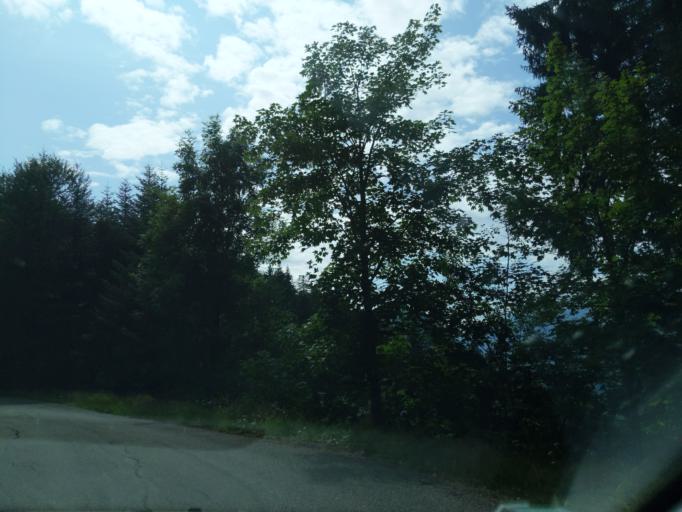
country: FR
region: Rhone-Alpes
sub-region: Departement de la Savoie
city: Ugine
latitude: 45.7463
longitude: 6.4695
